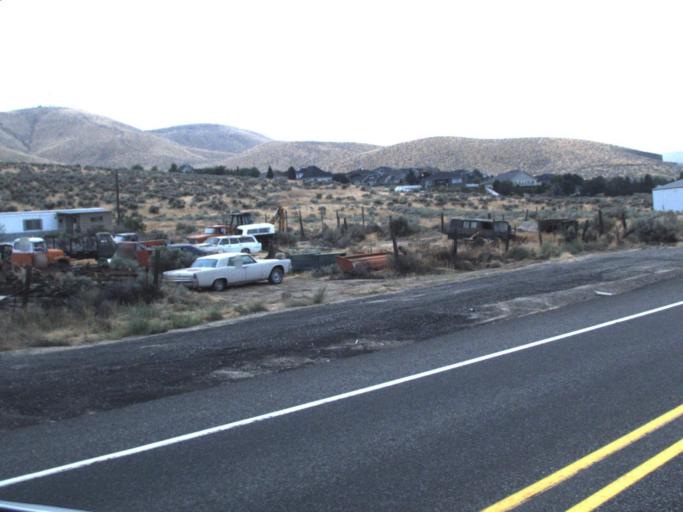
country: US
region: Washington
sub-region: Benton County
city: Prosser
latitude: 46.2065
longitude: -119.7448
